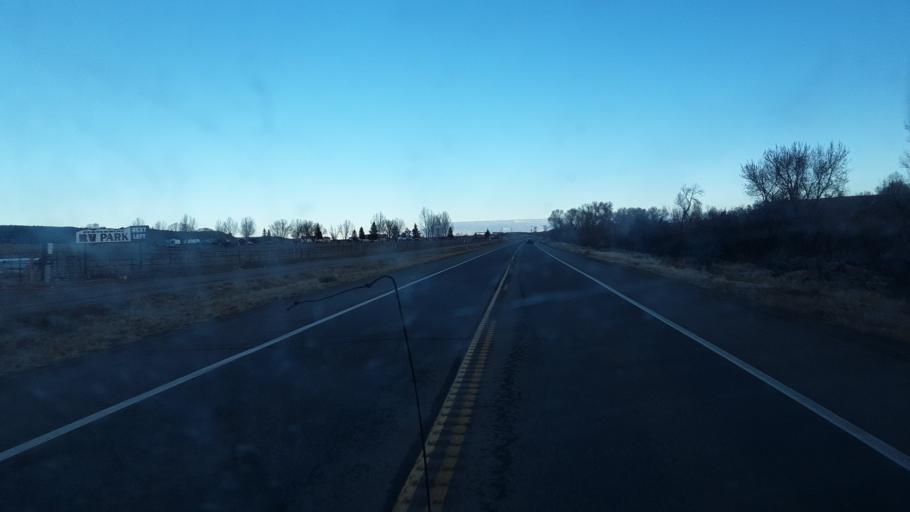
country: US
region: Colorado
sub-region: Montrose County
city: Montrose
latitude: 38.3382
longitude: -107.7866
